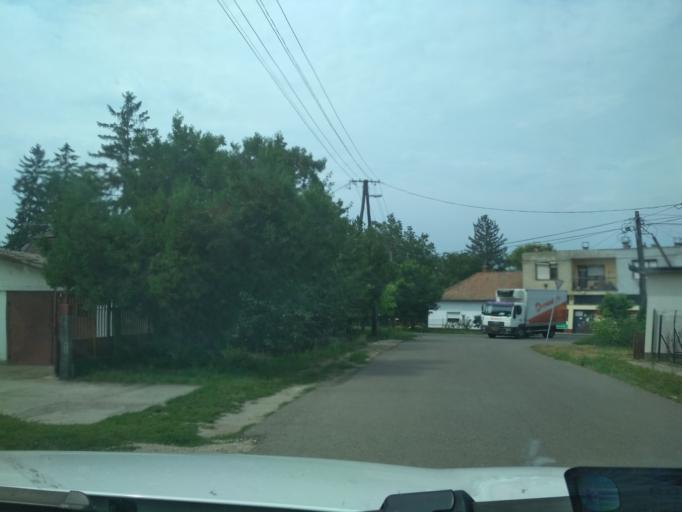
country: HU
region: Jasz-Nagykun-Szolnok
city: Tiszafured
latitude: 47.6248
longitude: 20.7549
